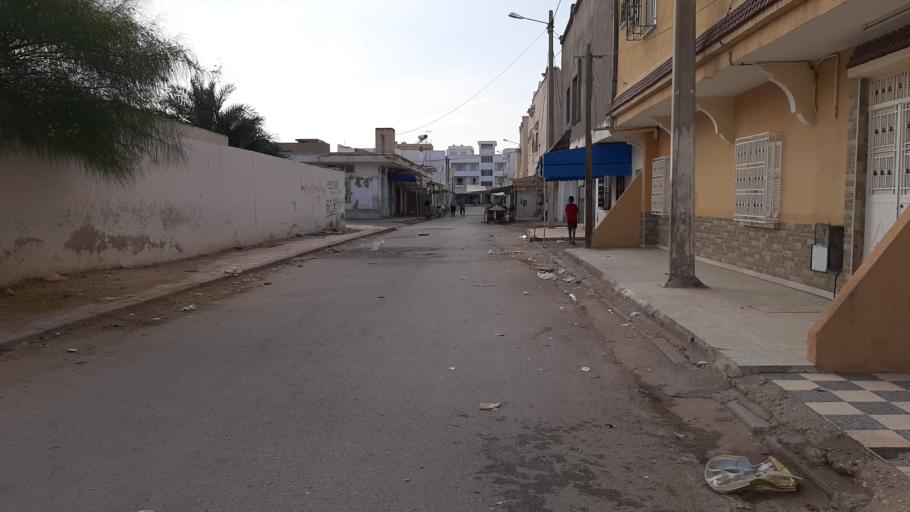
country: TN
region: Al Qayrawan
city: Kairouan
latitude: 35.6695
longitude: 10.0859
